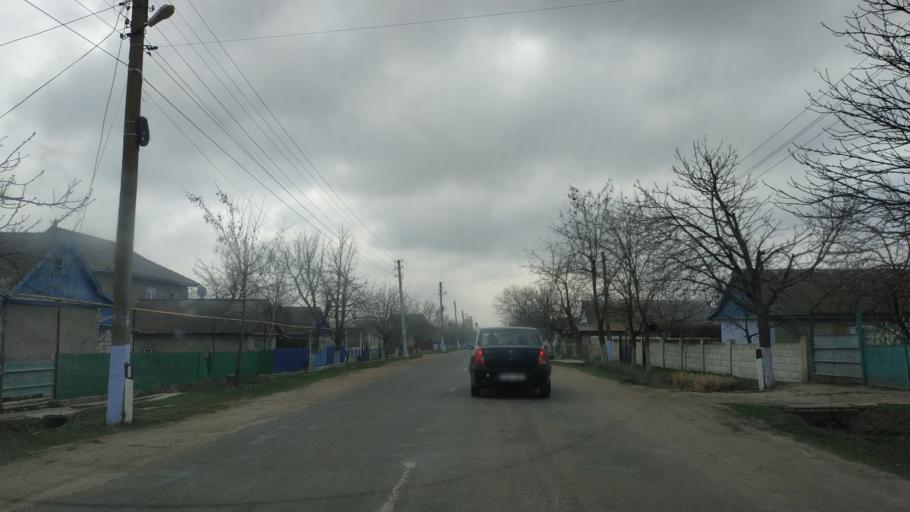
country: MD
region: Basarabeasca
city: Basarabeasca
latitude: 46.3753
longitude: 28.9232
